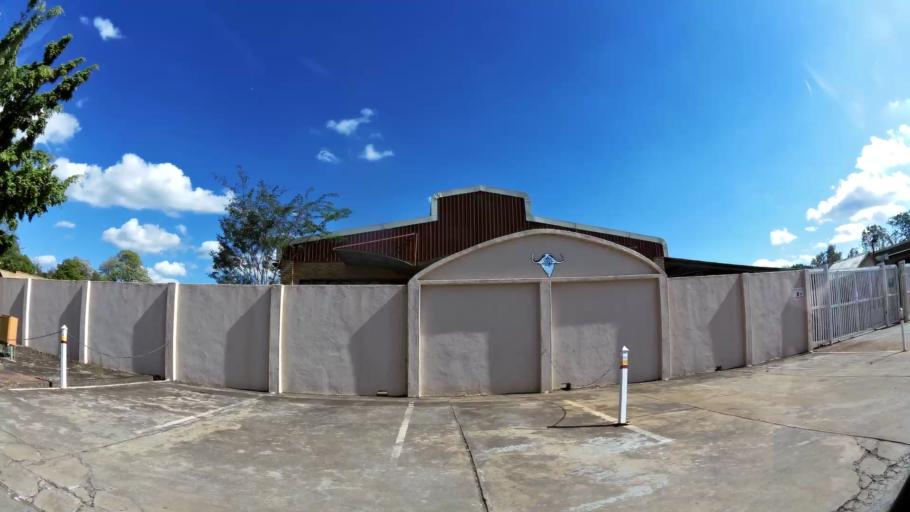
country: ZA
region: Limpopo
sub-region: Mopani District Municipality
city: Tzaneen
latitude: -23.8325
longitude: 30.1607
